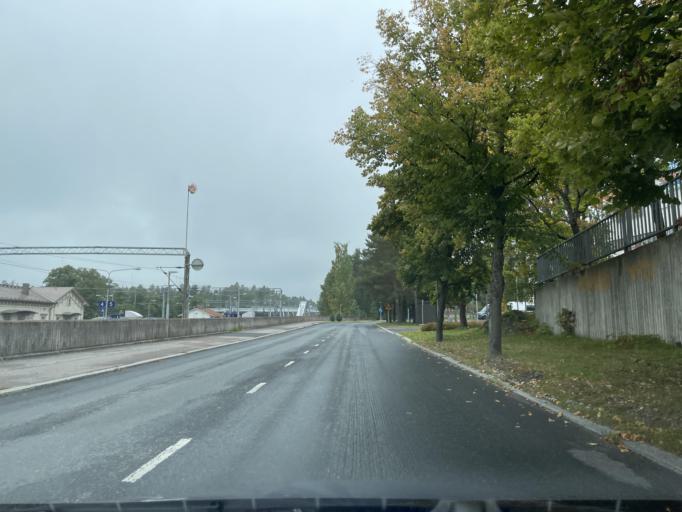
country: FI
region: Uusimaa
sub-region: Helsinki
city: Hyvinge
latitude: 60.6310
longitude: 24.8594
